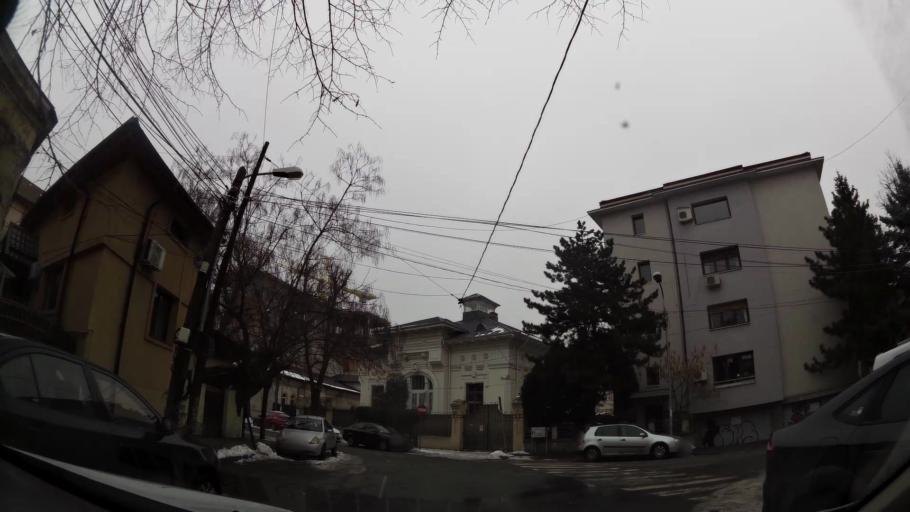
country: RO
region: Bucuresti
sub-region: Municipiul Bucuresti
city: Bucharest
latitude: 44.4444
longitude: 26.1070
